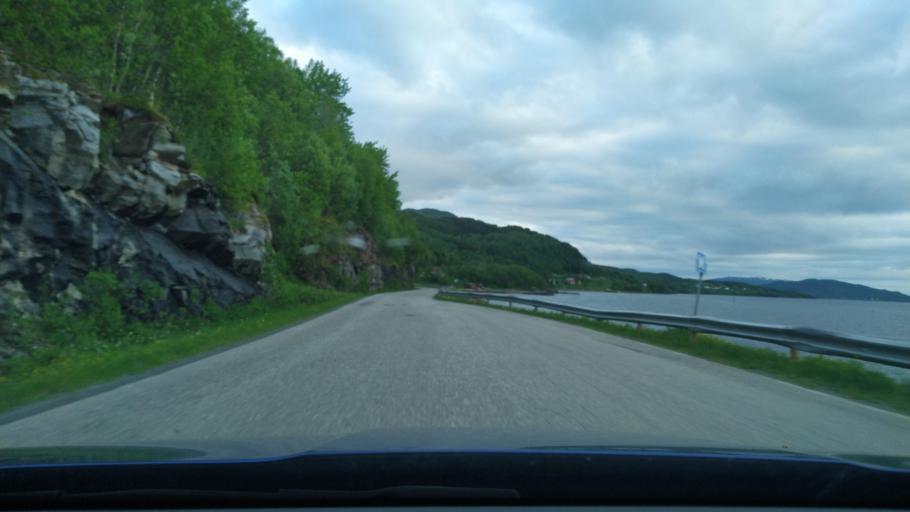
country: NO
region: Troms
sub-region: Lenvik
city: Finnsnes
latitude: 69.1404
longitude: 17.9110
